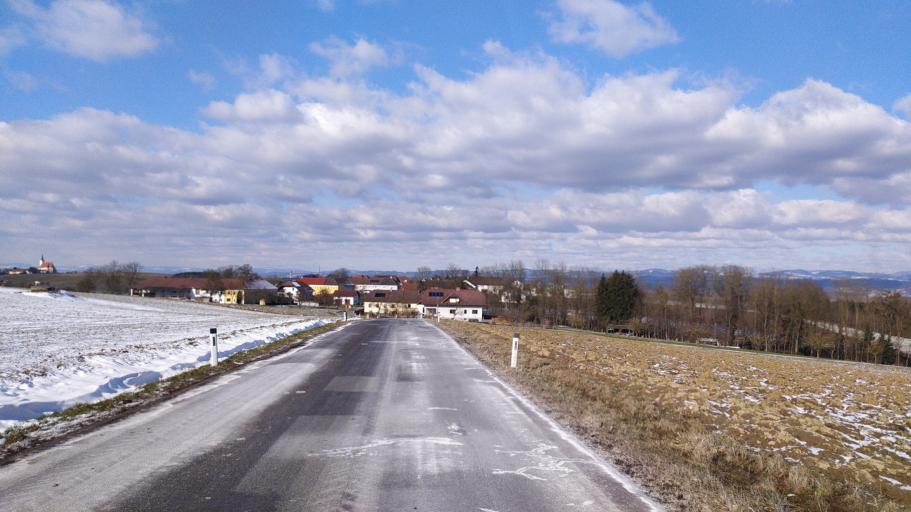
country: AT
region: Lower Austria
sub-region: Politischer Bezirk Amstetten
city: Zeillern
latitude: 48.1470
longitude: 14.7380
